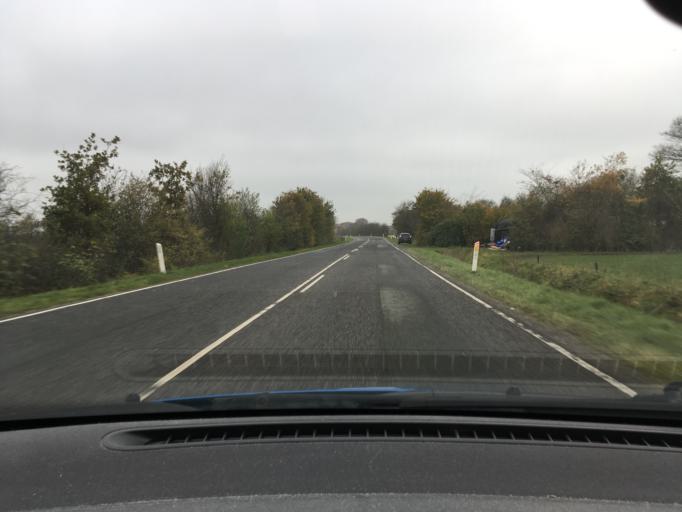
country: DK
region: South Denmark
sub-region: Aabenraa Kommune
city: Rodekro
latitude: 55.0707
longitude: 9.1901
